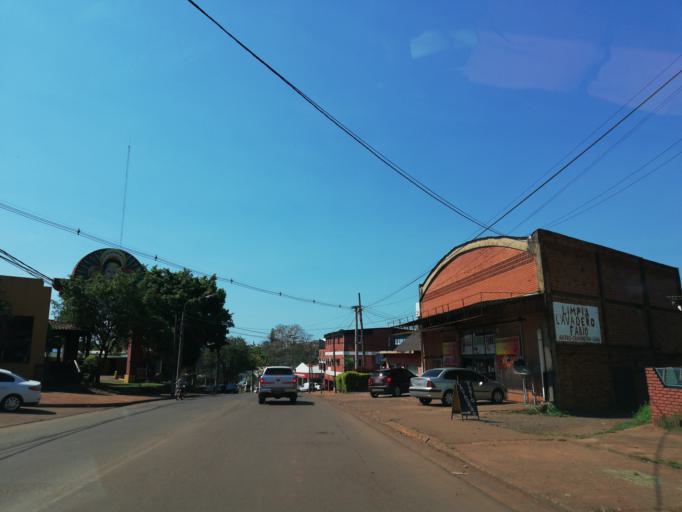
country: AR
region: Misiones
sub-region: Departamento de Eldorado
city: Eldorado
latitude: -26.4050
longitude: -54.6176
